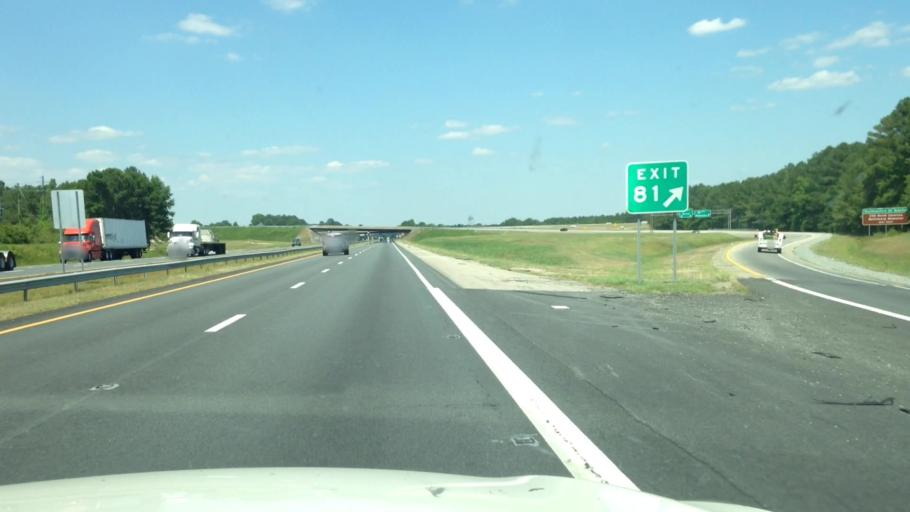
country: US
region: North Carolina
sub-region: Johnston County
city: Benson
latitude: 35.3858
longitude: -78.5247
